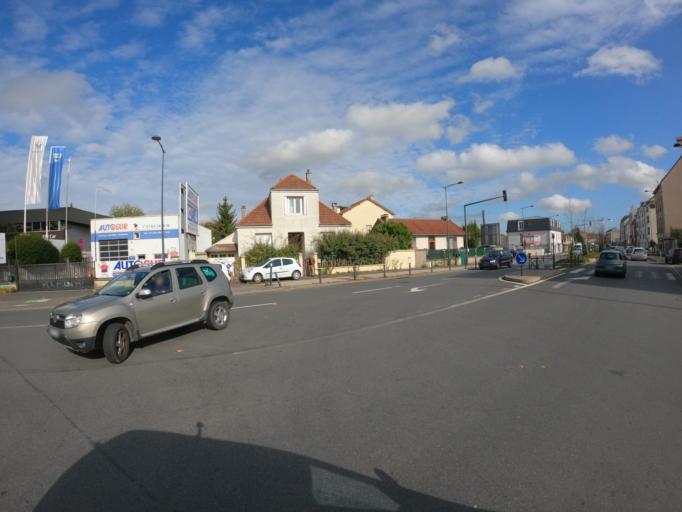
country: FR
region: Ile-de-France
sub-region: Departement de Seine-et-Marne
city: Brou-sur-Chantereine
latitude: 48.8790
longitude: 2.6229
